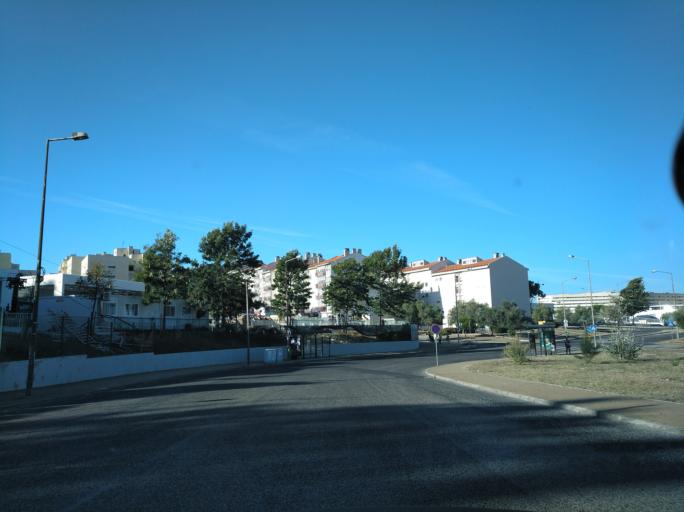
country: PT
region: Lisbon
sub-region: Loures
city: Moscavide
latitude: 38.7518
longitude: -9.1234
